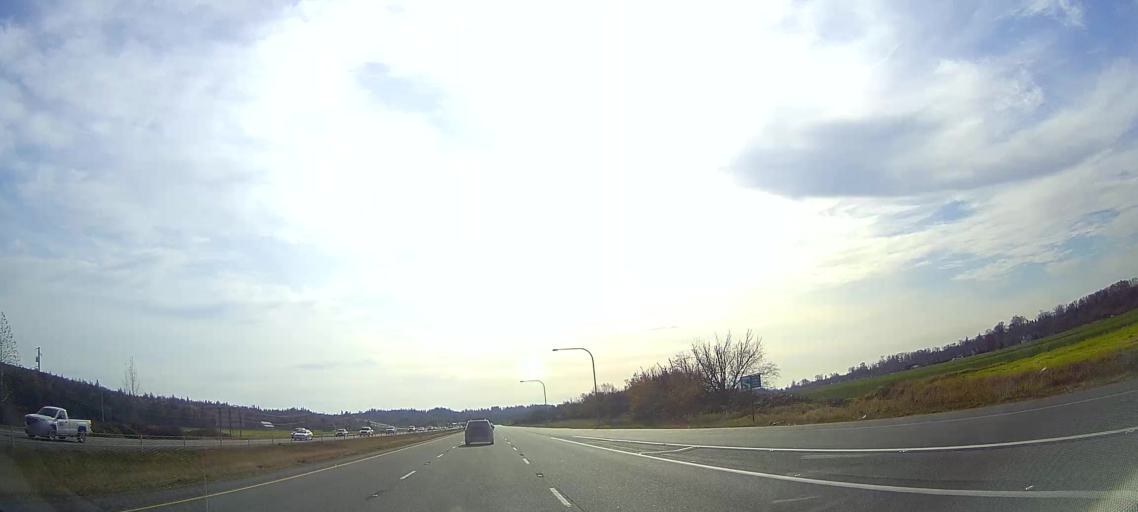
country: US
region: Washington
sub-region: Skagit County
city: Mount Vernon
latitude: 48.3380
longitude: -122.3354
